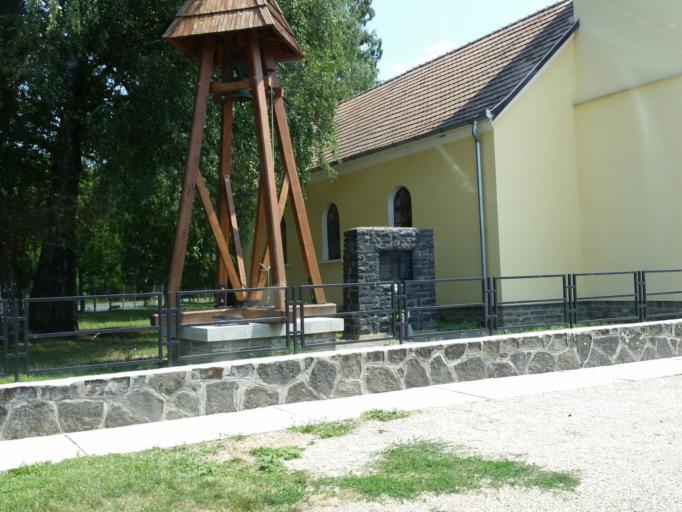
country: HU
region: Vas
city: Celldomolk
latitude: 47.2690
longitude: 17.0997
